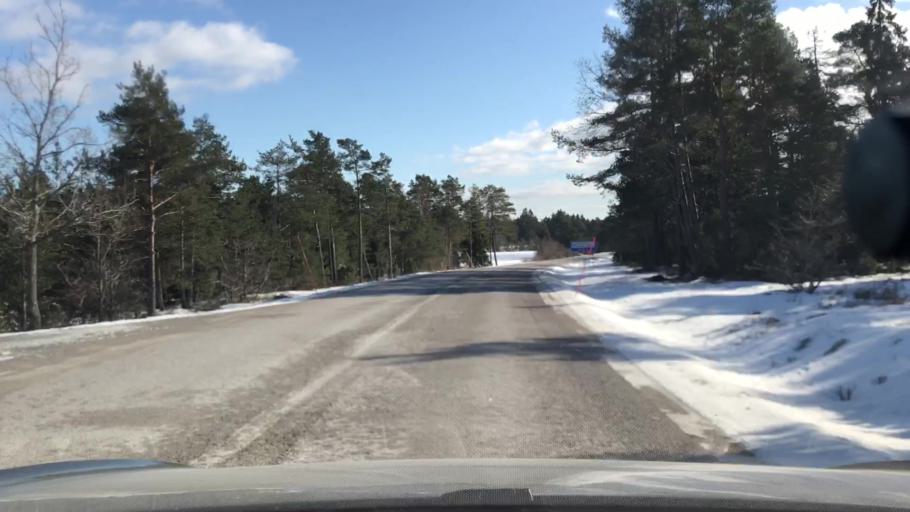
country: SE
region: Gotland
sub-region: Gotland
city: Hemse
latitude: 57.3462
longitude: 18.6926
